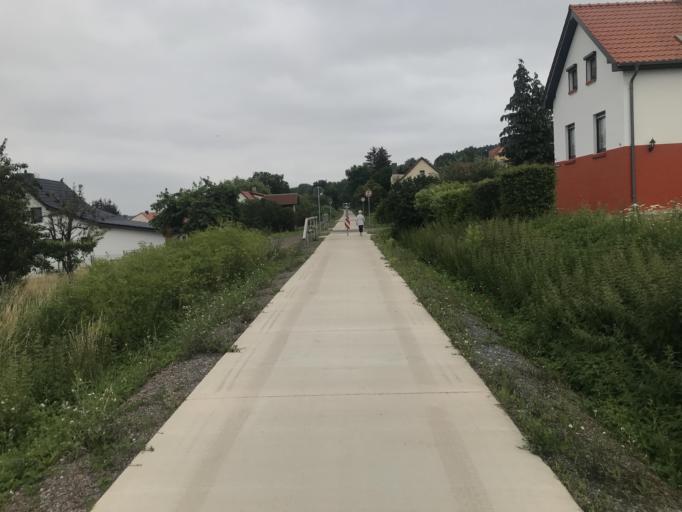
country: DE
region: Saxony-Anhalt
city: Rieder
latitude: 51.7301
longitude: 11.1632
